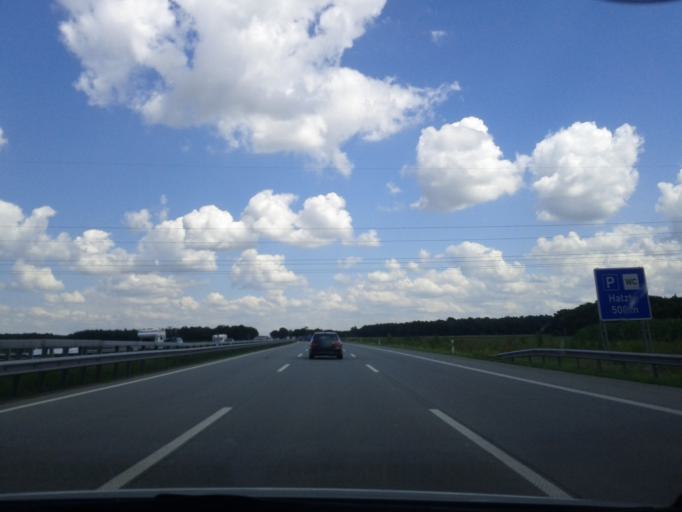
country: DE
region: Lower Saxony
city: Gross Meckelsen
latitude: 53.2496
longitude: 9.4187
